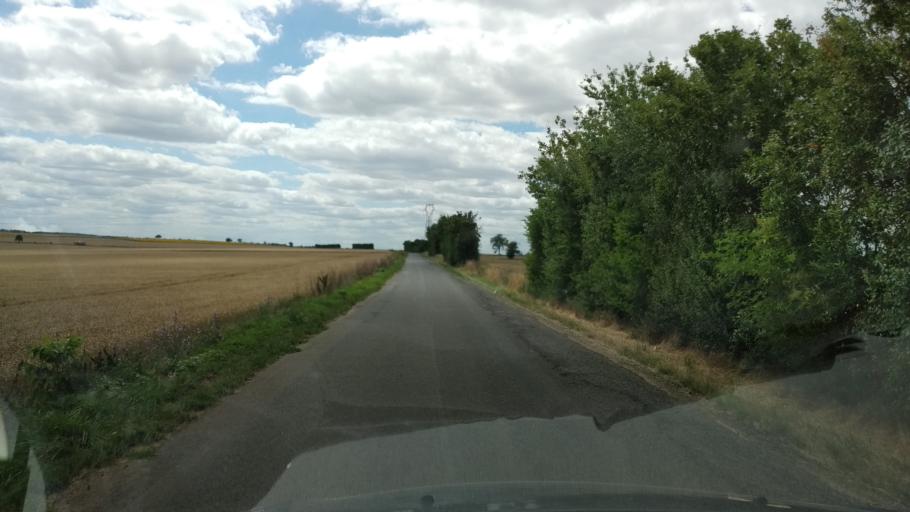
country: FR
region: Poitou-Charentes
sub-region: Departement de la Vienne
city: Jaunay-Clan
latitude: 46.6782
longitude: 0.3502
